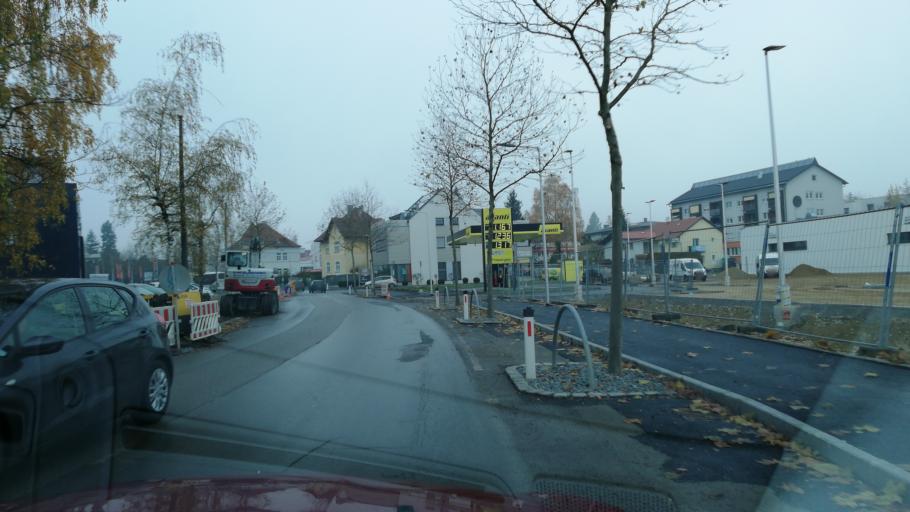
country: AT
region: Upper Austria
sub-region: Politischer Bezirk Ried im Innkreis
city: Ried im Innkreis
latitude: 48.2127
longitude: 13.4854
